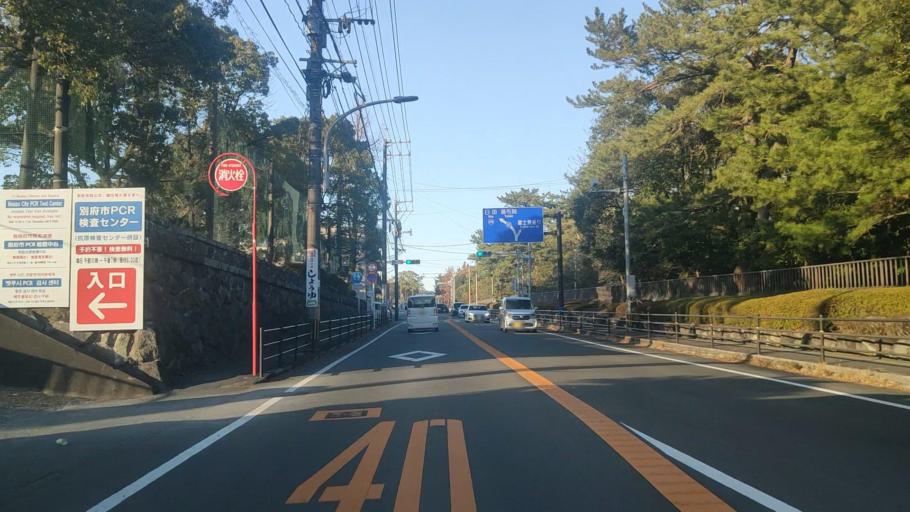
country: JP
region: Oita
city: Beppu
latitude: 33.2803
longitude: 131.4890
